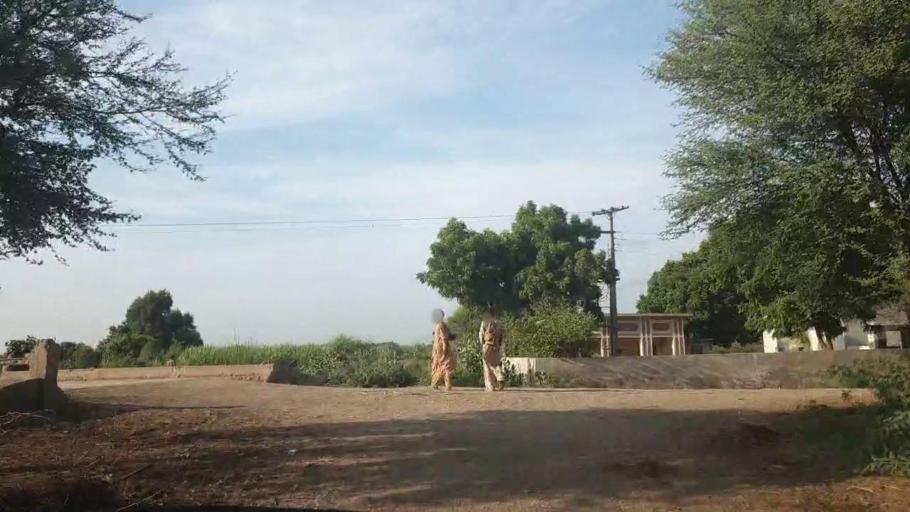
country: PK
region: Sindh
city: Tando Muhammad Khan
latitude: 25.2314
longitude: 68.5361
